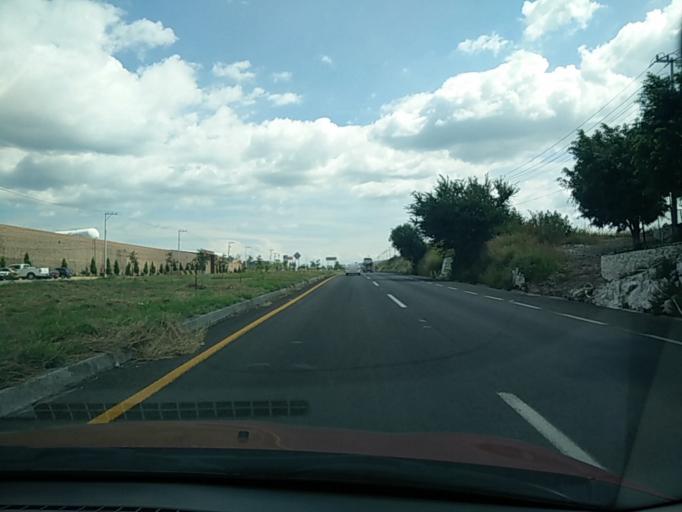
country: MX
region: Jalisco
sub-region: Ixtlahuacan de los Membrillos
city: Los Olivos
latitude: 20.4479
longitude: -103.2476
